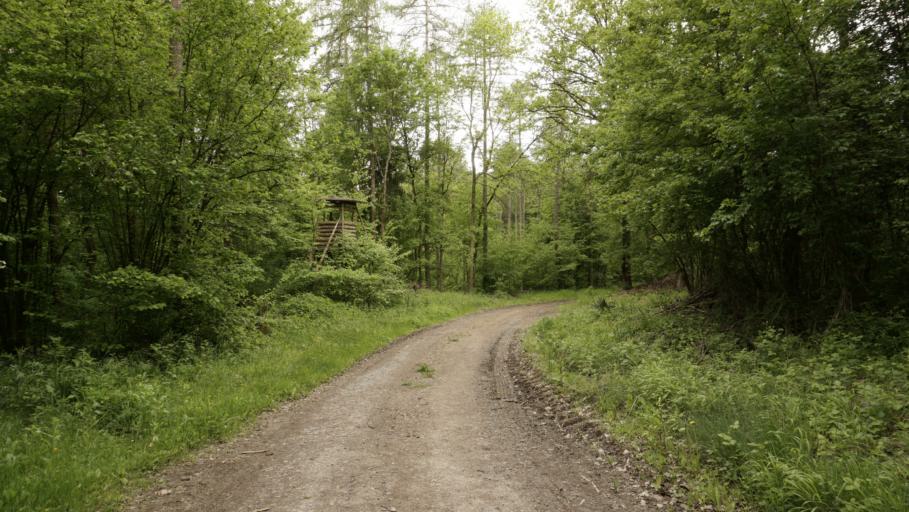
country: DE
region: Baden-Wuerttemberg
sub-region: Karlsruhe Region
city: Mosbach
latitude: 49.3684
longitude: 9.1685
